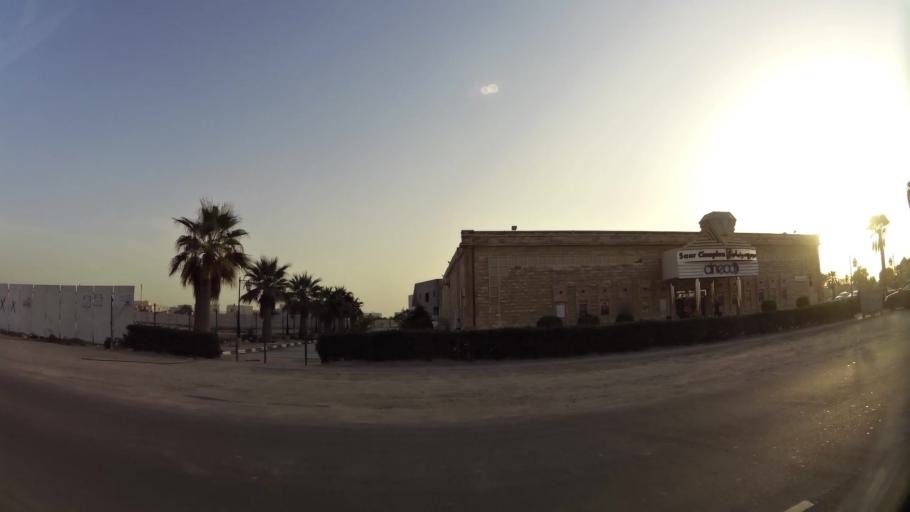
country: BH
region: Northern
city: Madinat `Isa
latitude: 26.1961
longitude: 50.4783
